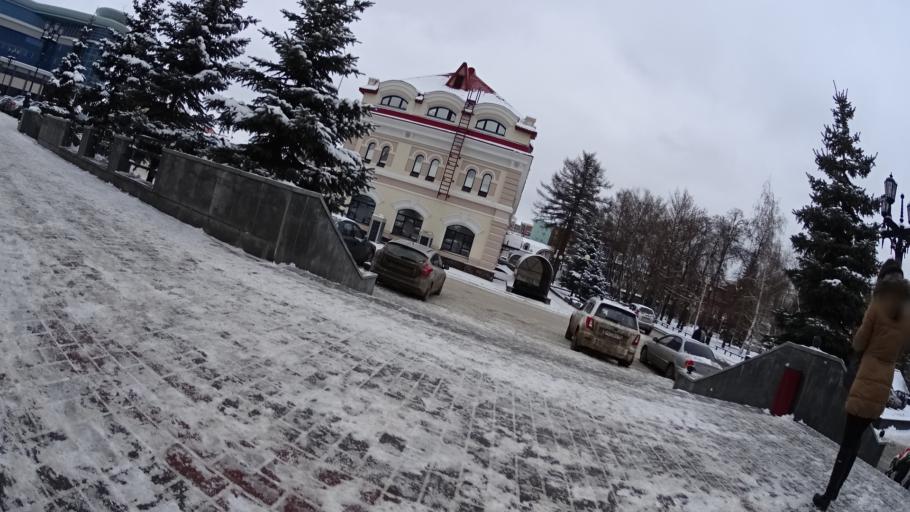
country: RU
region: Bashkortostan
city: Ufa
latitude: 54.7252
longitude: 55.9451
